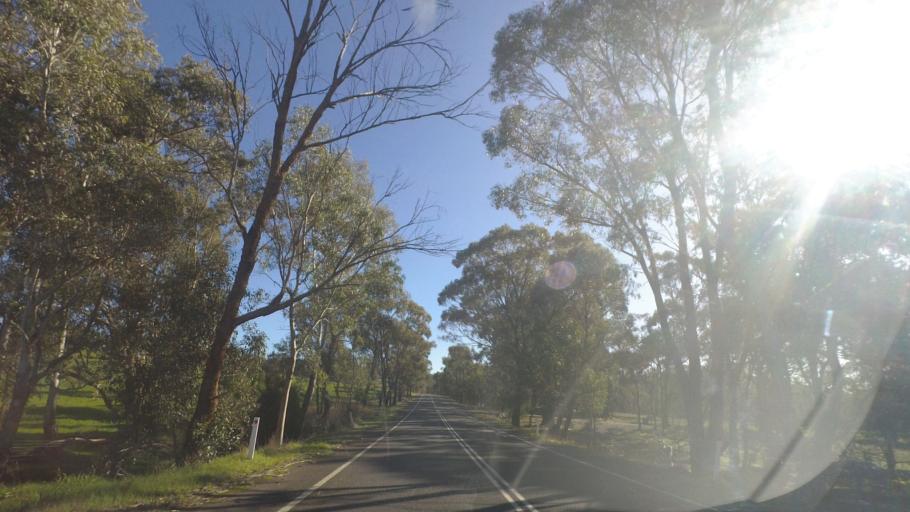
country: AU
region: Victoria
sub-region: Greater Bendigo
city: Kennington
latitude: -36.9198
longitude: 144.3403
